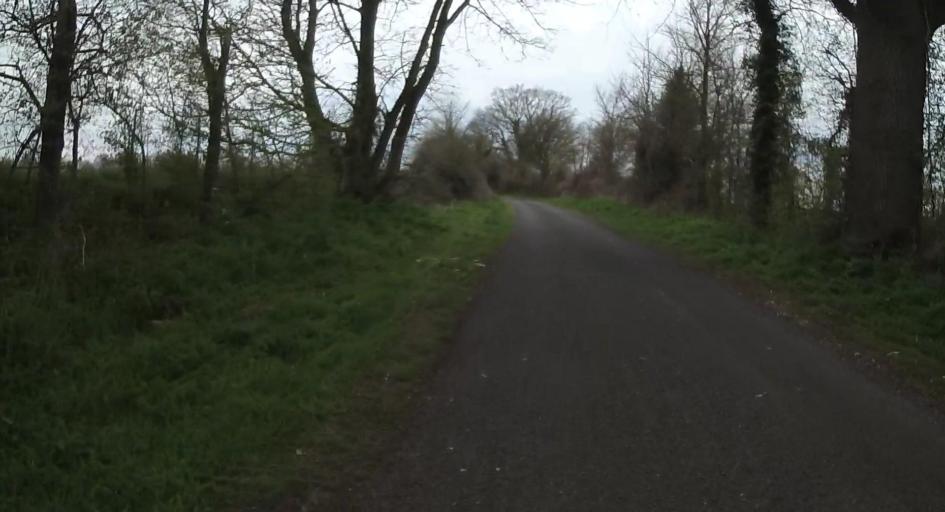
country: GB
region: England
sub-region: Hampshire
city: Long Sutton
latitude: 51.2285
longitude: -0.9667
